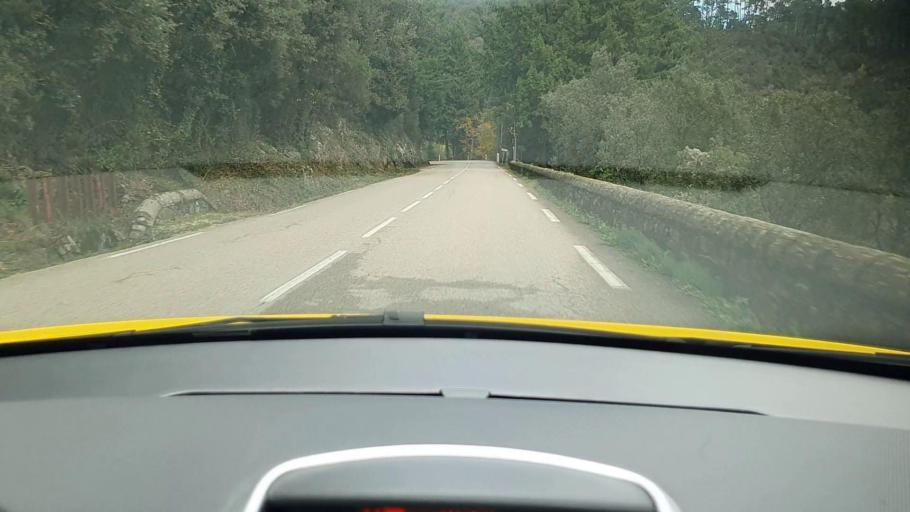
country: FR
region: Languedoc-Roussillon
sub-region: Departement du Gard
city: Saint-Jean-du-Gard
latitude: 44.1077
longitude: 3.8113
